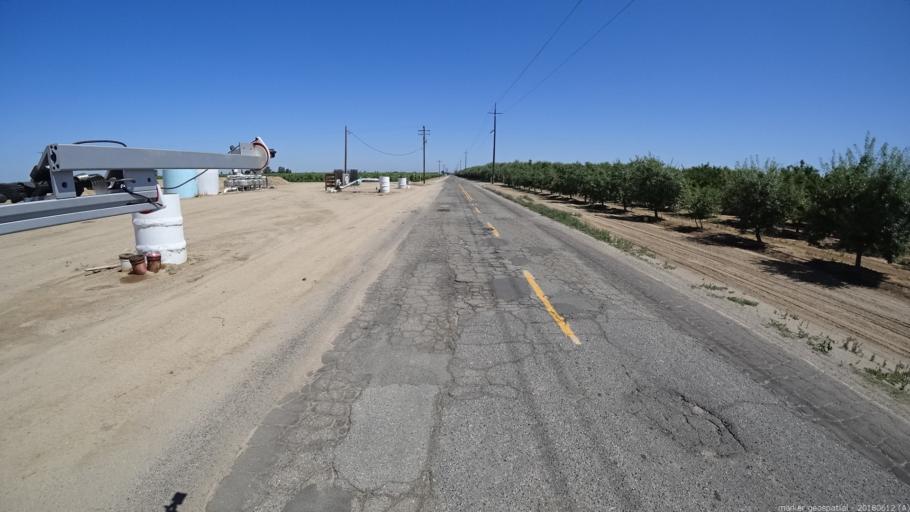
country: US
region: California
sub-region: Madera County
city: Chowchilla
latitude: 37.0247
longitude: -120.3286
